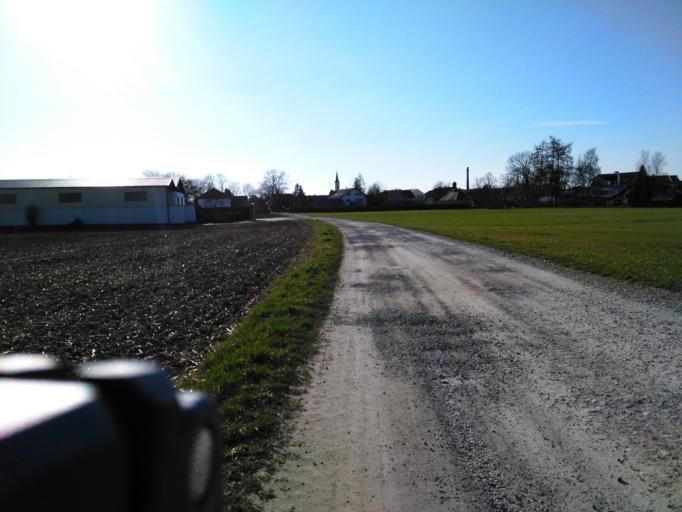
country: DE
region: Bavaria
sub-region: Upper Bavaria
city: Mammendorf
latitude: 48.2060
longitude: 11.1641
